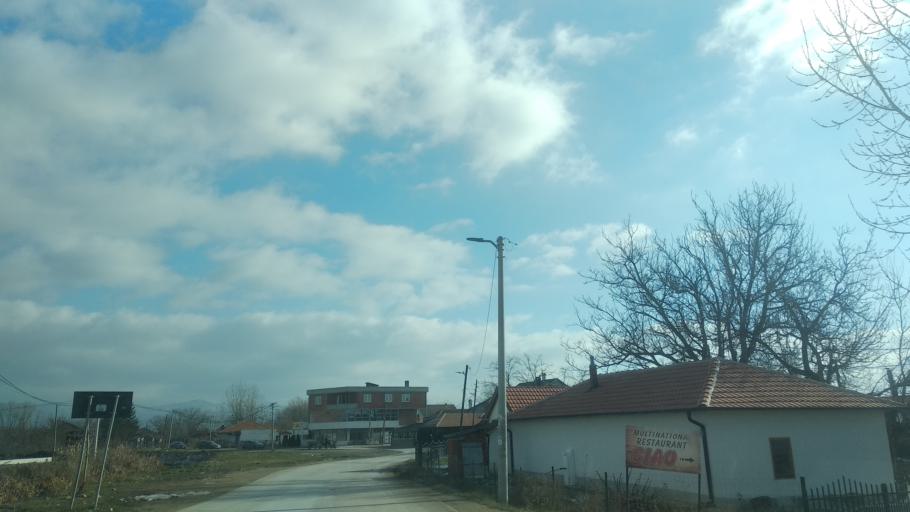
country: XK
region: Pristina
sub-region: Lipjan
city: Lipljan
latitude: 42.5942
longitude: 21.1394
